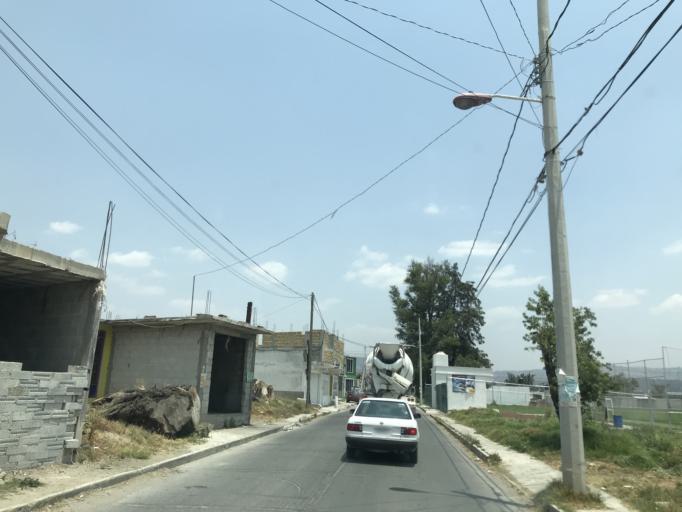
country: MX
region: Tlaxcala
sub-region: Ixtacuixtla de Mariano Matamoros
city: Villa Mariano Matamoros
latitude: 19.3133
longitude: -98.3726
